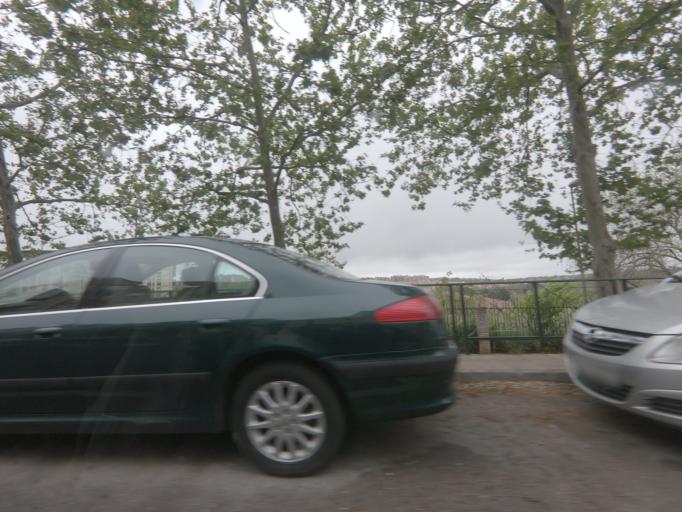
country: ES
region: Extremadura
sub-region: Provincia de Caceres
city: Caceres
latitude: 39.4759
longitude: -6.3795
